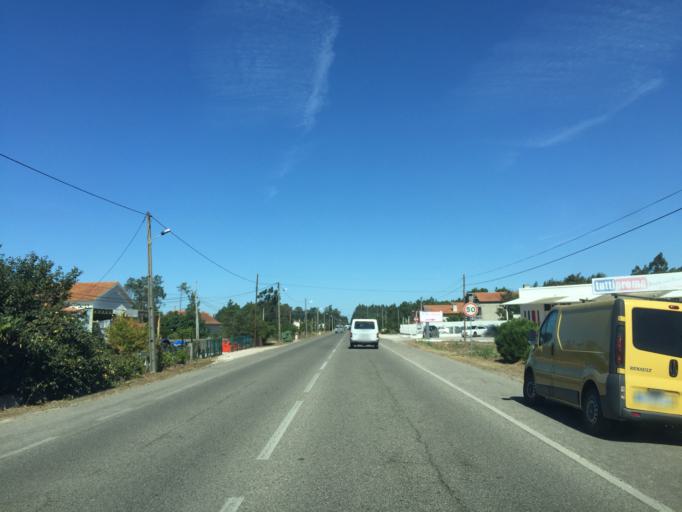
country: PT
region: Coimbra
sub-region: Figueira da Foz
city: Alhadas
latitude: 40.2824
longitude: -8.7704
